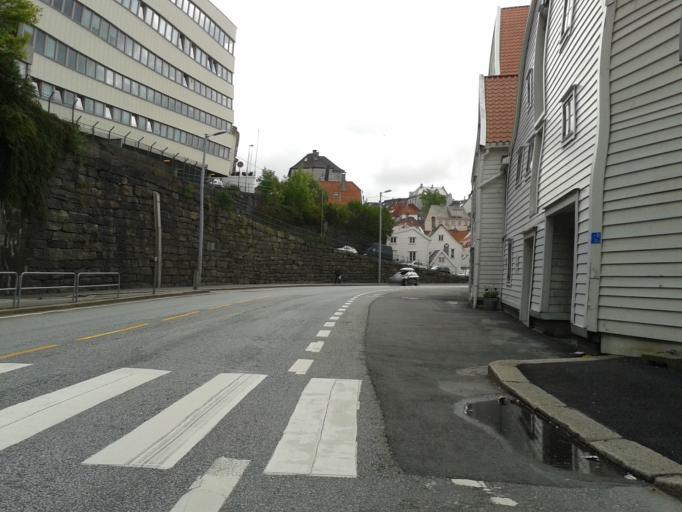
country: NO
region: Hordaland
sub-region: Bergen
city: Bergen
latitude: 60.4037
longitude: 5.3210
